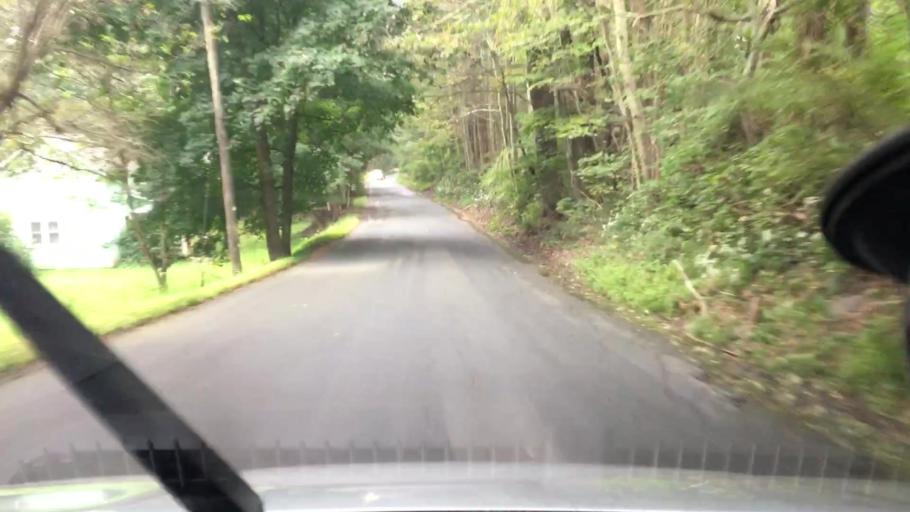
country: US
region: Pennsylvania
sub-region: Monroe County
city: Mountainhome
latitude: 41.1670
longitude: -75.2712
